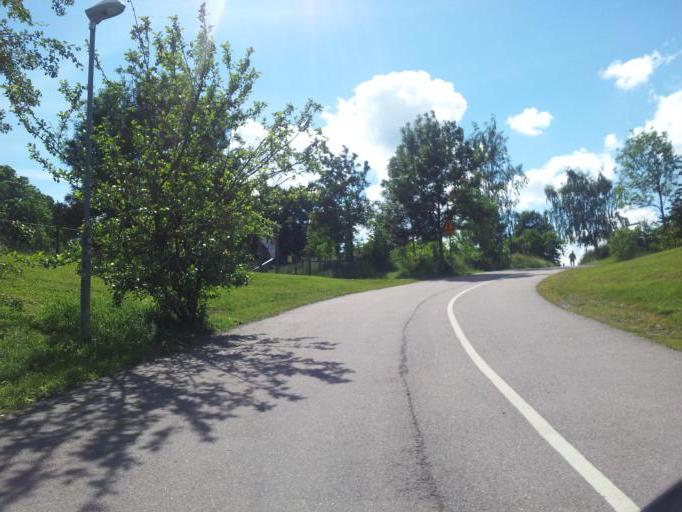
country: SE
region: Uppsala
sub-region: Uppsala Kommun
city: Uppsala
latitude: 59.8760
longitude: 17.6718
